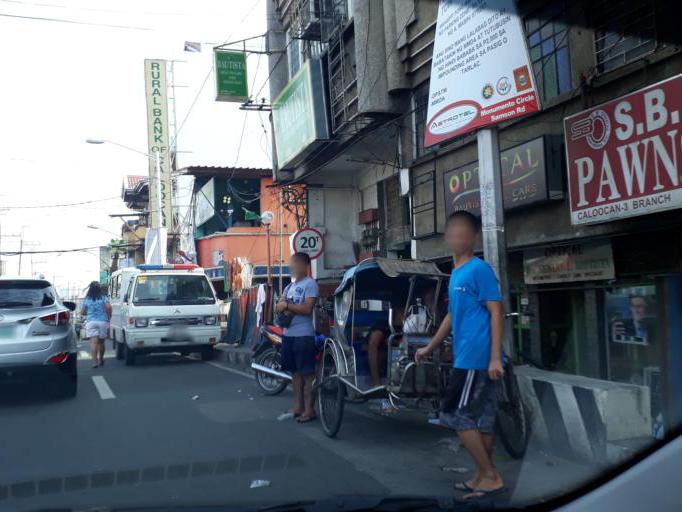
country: PH
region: Metro Manila
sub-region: Caloocan City
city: Niugan
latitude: 14.6374
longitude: 120.9755
